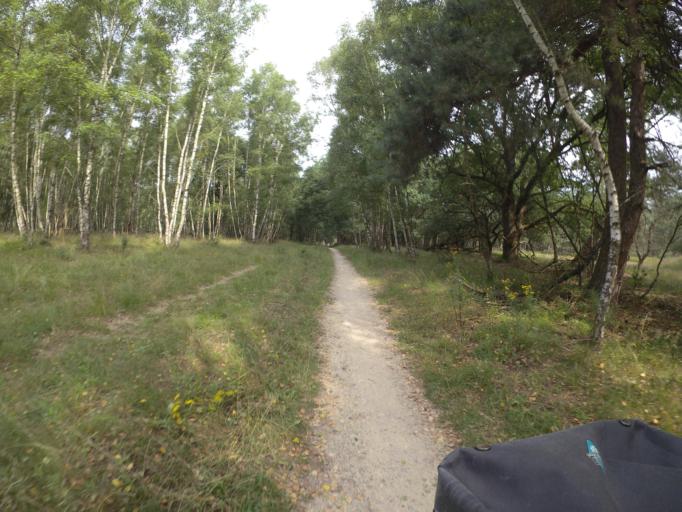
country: NL
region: Gelderland
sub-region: Gemeente Ede
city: Otterlo
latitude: 52.0618
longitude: 5.7667
